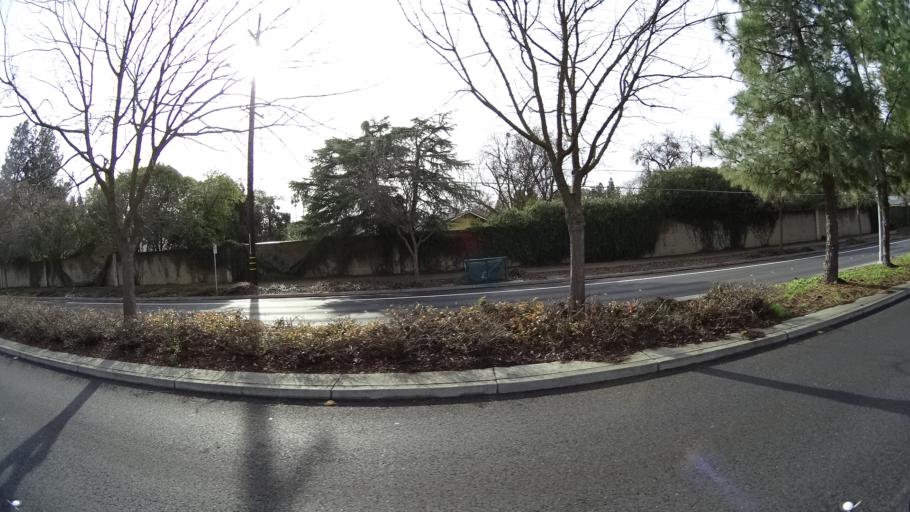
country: US
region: California
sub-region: Yolo County
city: Davis
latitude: 38.5637
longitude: -121.7153
